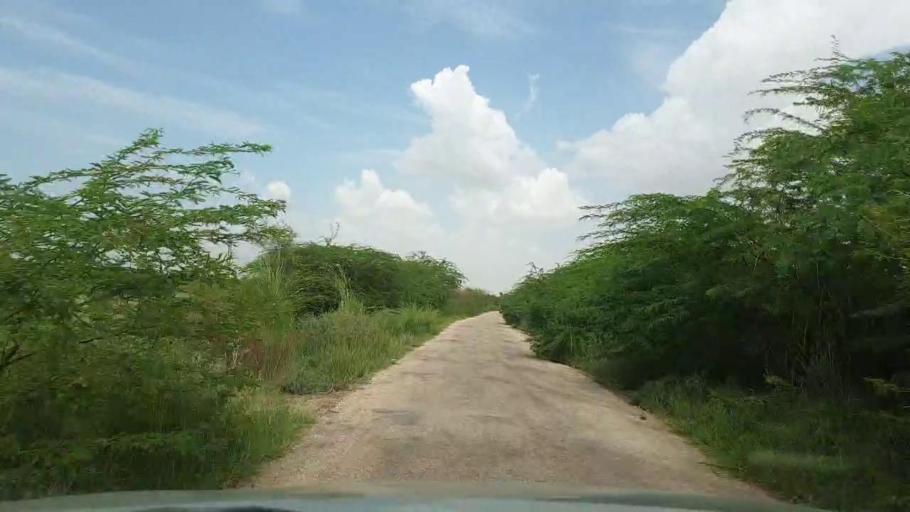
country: PK
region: Sindh
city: Bozdar
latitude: 27.0251
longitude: 68.9514
